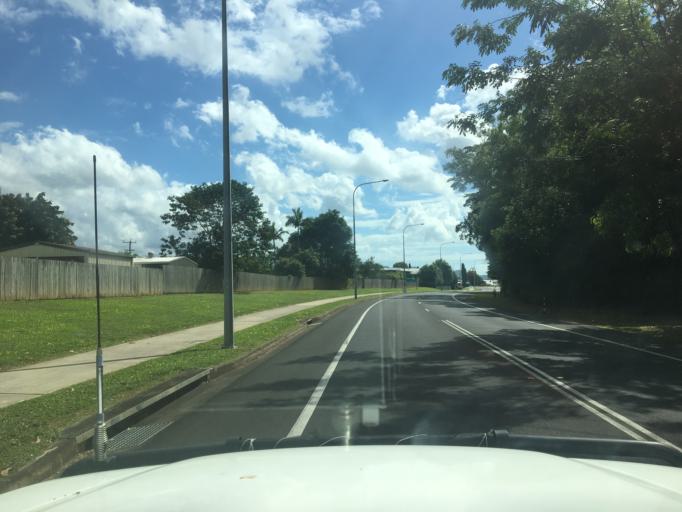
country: AU
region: Queensland
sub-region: Cairns
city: Woree
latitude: -16.9656
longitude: 145.7463
